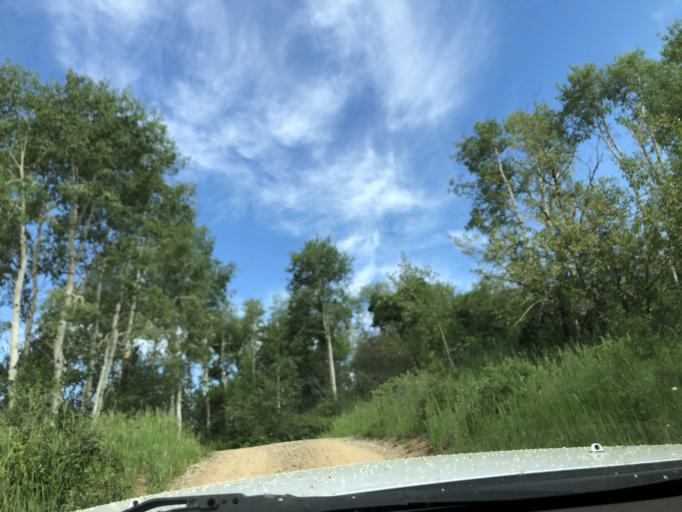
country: US
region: Colorado
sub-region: Delta County
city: Paonia
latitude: 39.0349
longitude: -107.3357
